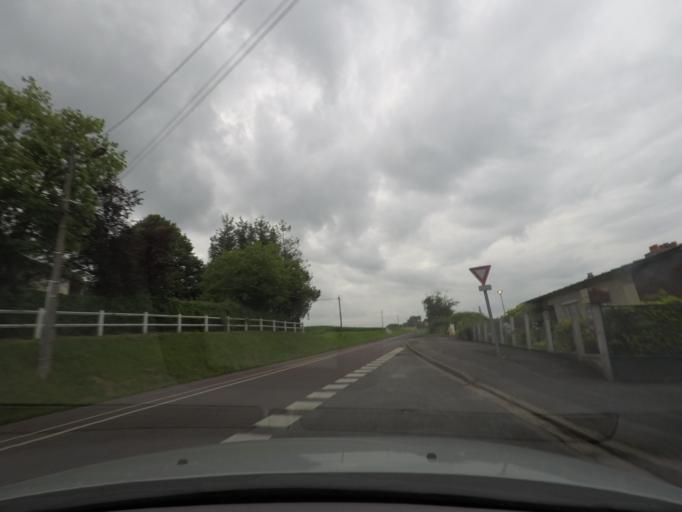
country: FR
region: Haute-Normandie
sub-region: Departement de la Seine-Maritime
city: Neufchatel-en-Bray
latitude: 49.7318
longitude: 1.4543
